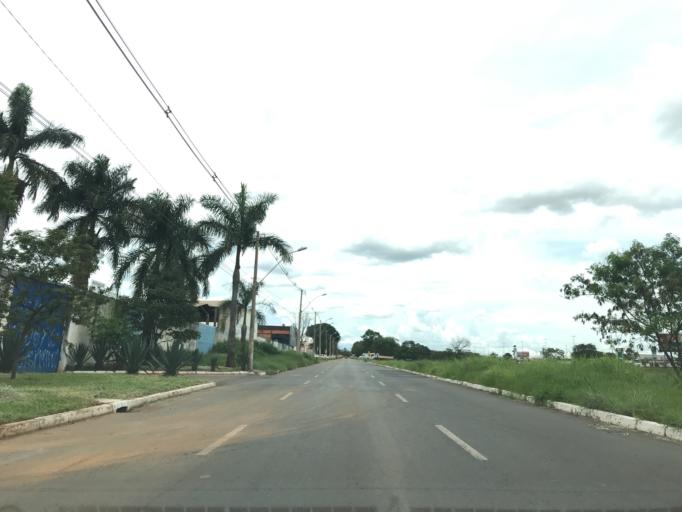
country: BR
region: Federal District
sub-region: Brasilia
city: Brasilia
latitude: -15.7900
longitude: -47.9836
